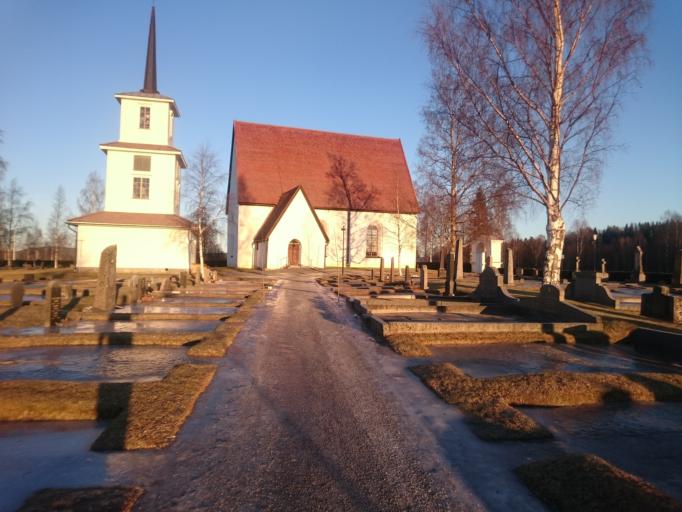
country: SE
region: Vaesternorrland
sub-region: OErnskoeldsviks Kommun
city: Bjasta
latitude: 63.2905
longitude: 18.2946
